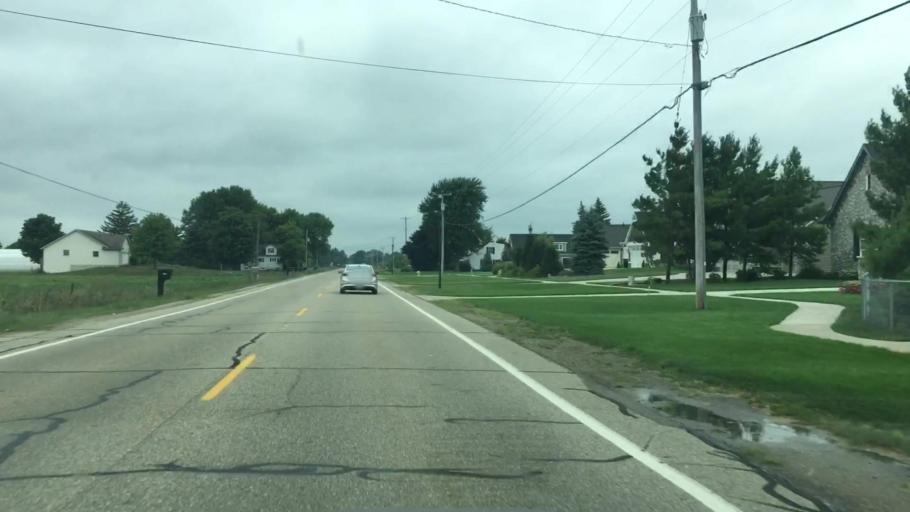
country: US
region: Michigan
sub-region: Ottawa County
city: Hudsonville
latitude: 42.8708
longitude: -85.8290
